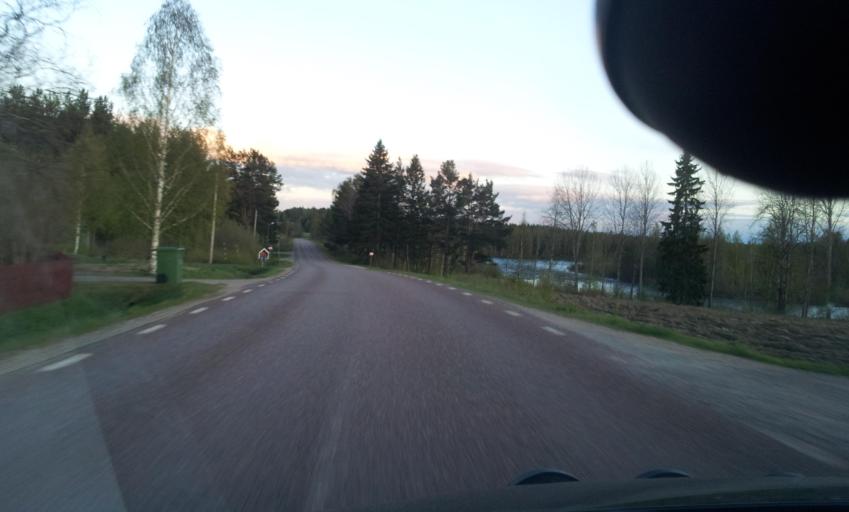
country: SE
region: Gaevleborg
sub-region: Bollnas Kommun
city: Bollnas
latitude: 61.3860
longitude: 16.4006
